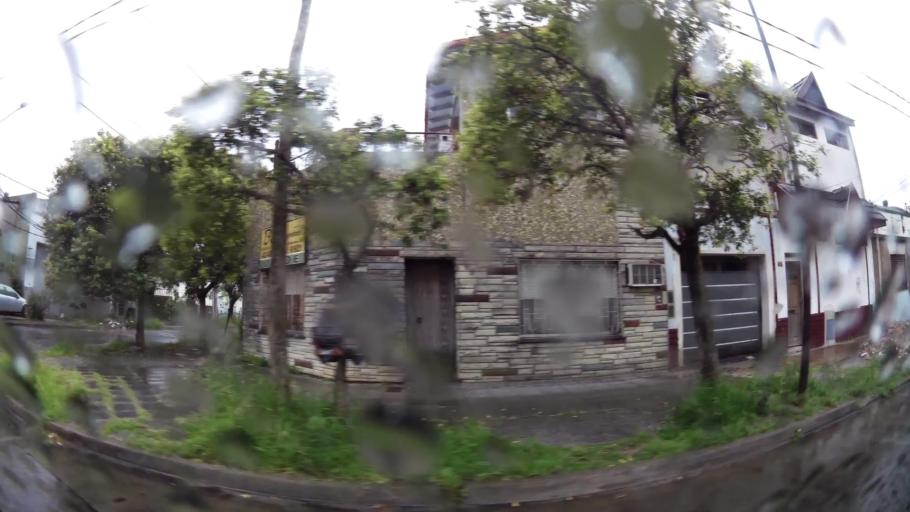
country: AR
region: Buenos Aires
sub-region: Partido de Lanus
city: Lanus
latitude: -34.7025
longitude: -58.4033
